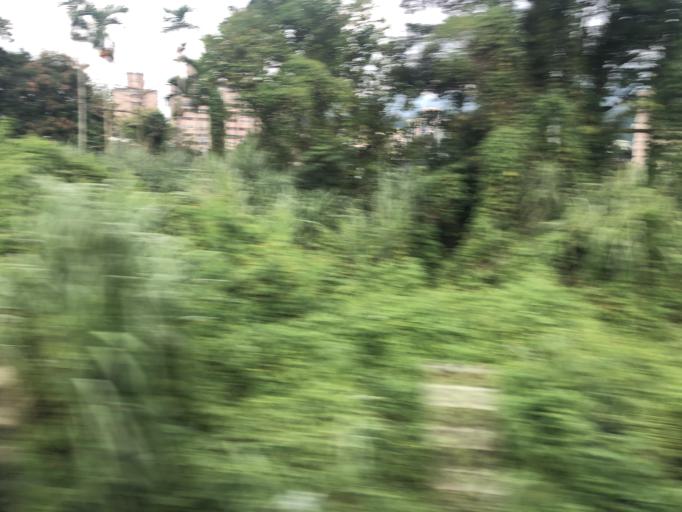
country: TW
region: Taiwan
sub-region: Taoyuan
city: Taoyuan
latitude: 24.9216
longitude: 121.3640
